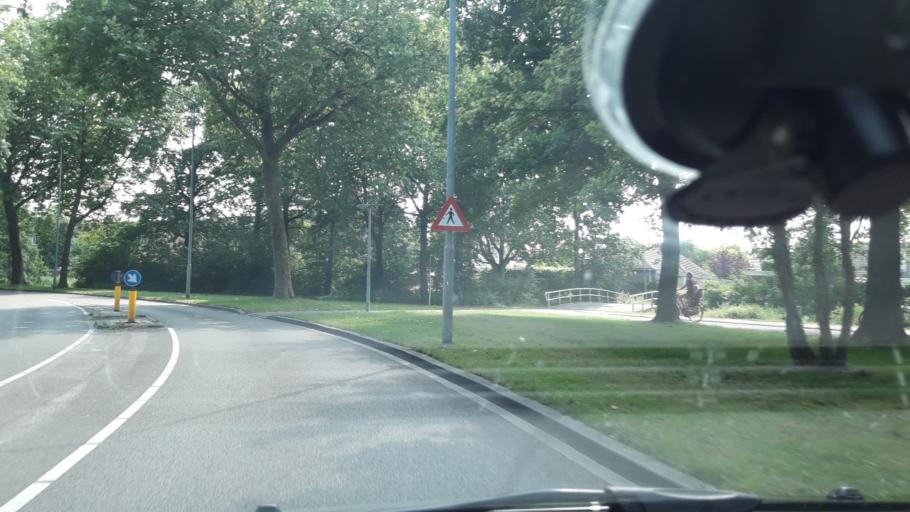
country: NL
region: Gelderland
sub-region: Gemeente Harderwijk
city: Harderwijk
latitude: 52.3446
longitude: 5.6129
